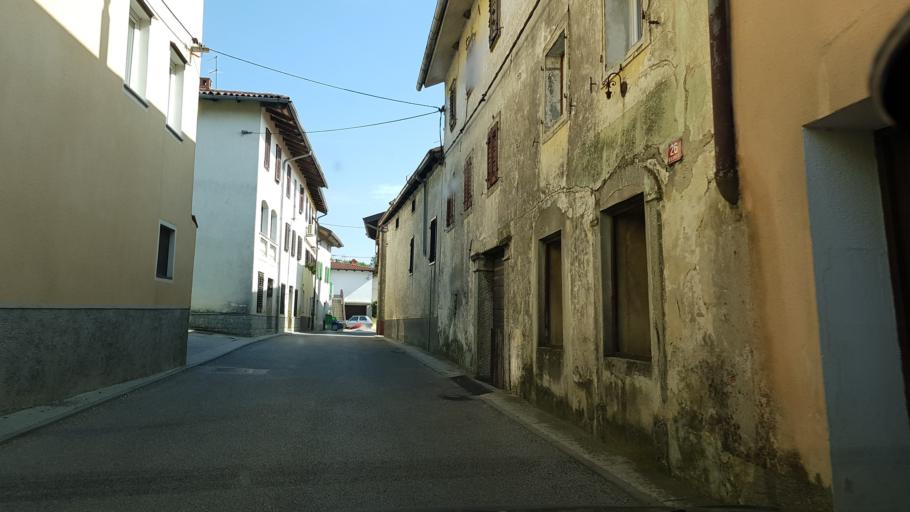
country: IT
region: Friuli Venezia Giulia
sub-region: Provincia di Gorizia
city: San Floriano del Collio
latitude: 46.0068
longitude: 13.5752
